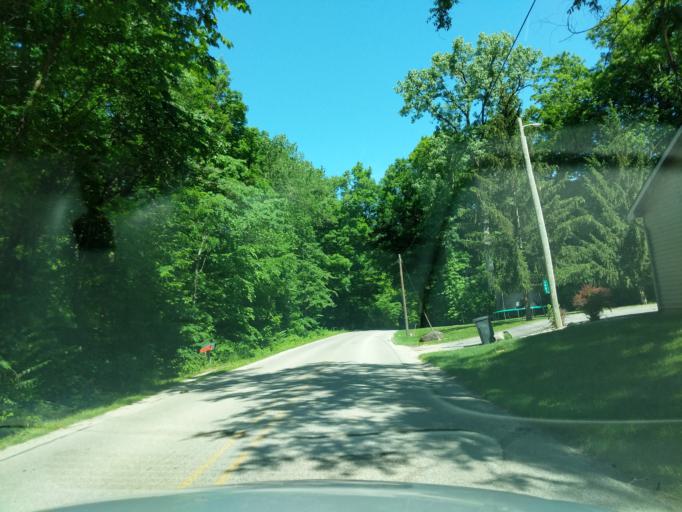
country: US
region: Indiana
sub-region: Huntington County
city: Huntington
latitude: 40.8513
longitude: -85.5092
